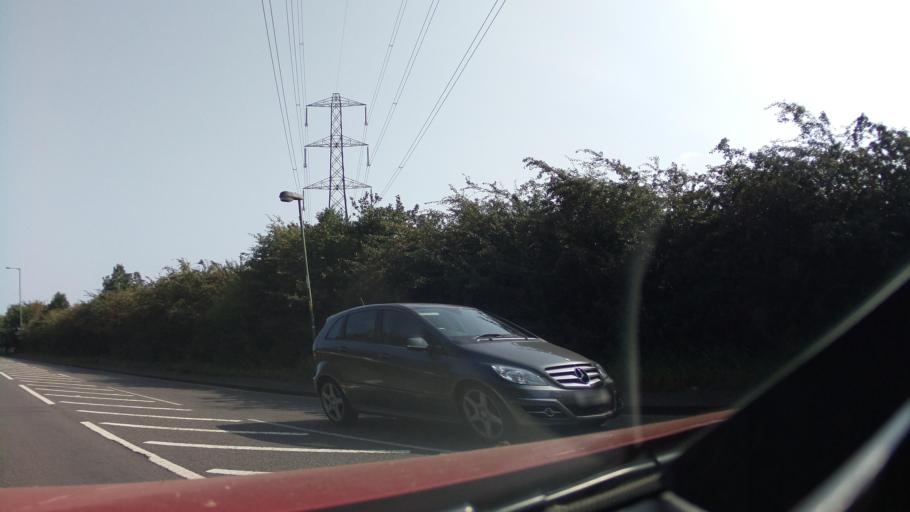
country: GB
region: England
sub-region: Walsall
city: Streetly
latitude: 52.6052
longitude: -1.8884
